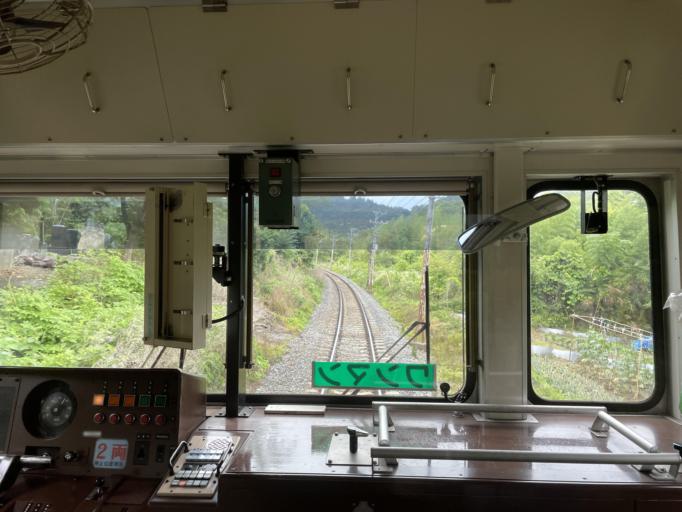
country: JP
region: Saitama
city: Kodamacho-kodamaminami
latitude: 36.1312
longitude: 139.1405
